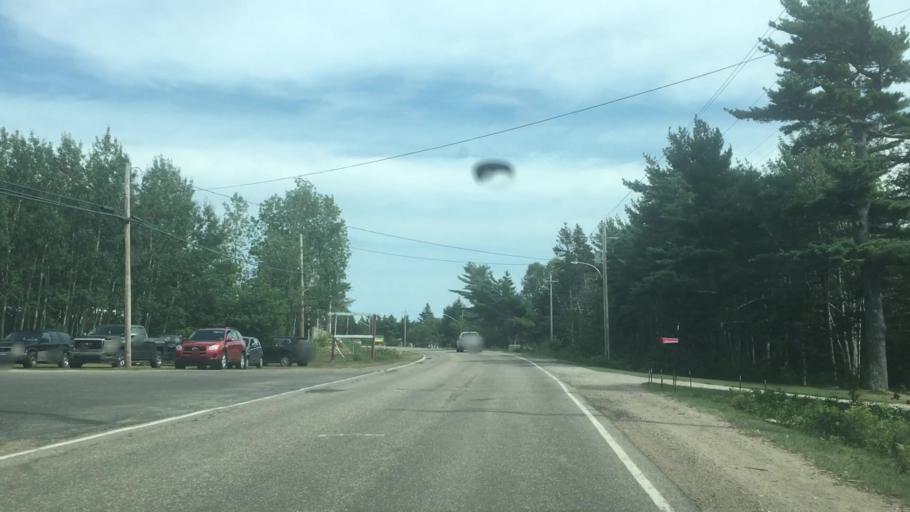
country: CA
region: Nova Scotia
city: Sydney Mines
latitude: 46.6899
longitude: -60.3926
